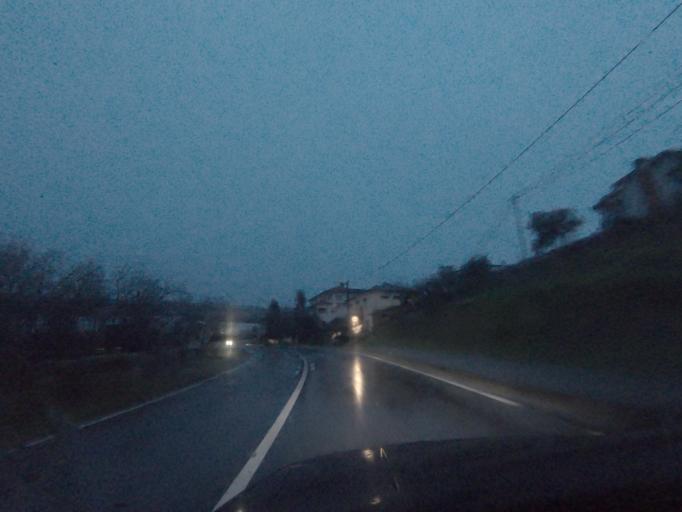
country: PT
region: Vila Real
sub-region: Vila Real
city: Vila Real
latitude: 41.2866
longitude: -7.7028
